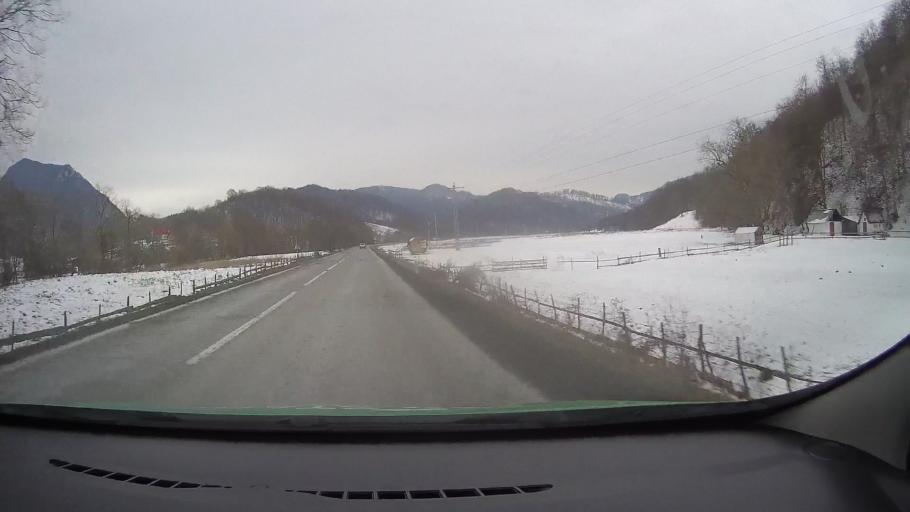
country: RO
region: Brasov
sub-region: Oras Rasnov
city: Rasnov
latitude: 45.5490
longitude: 25.4939
